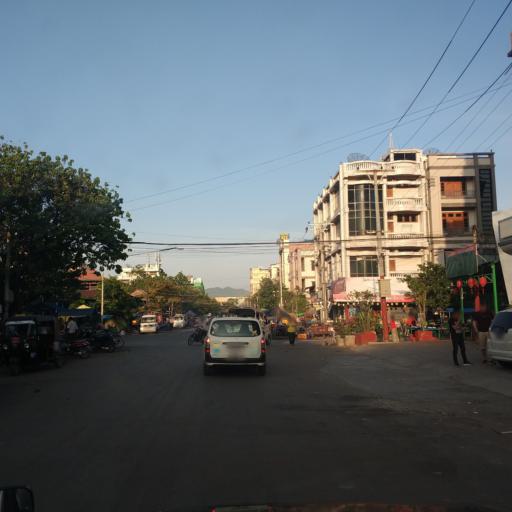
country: MM
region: Mandalay
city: Mandalay
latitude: 21.9751
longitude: 96.0901
